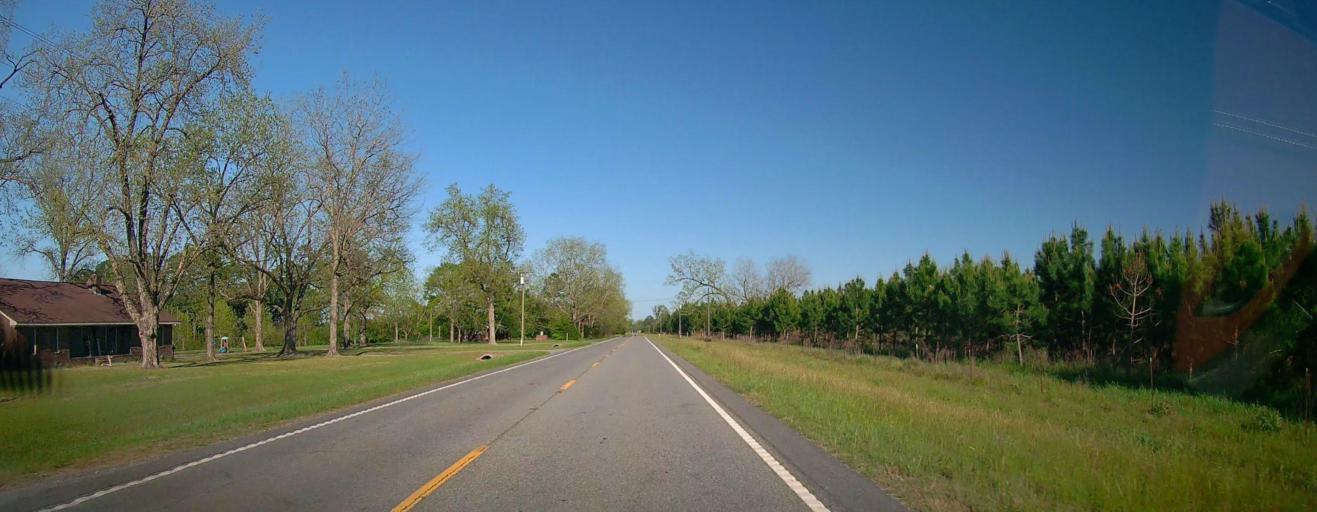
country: US
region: Georgia
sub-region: Ben Hill County
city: Fitzgerald
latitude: 31.7182
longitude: -83.3216
